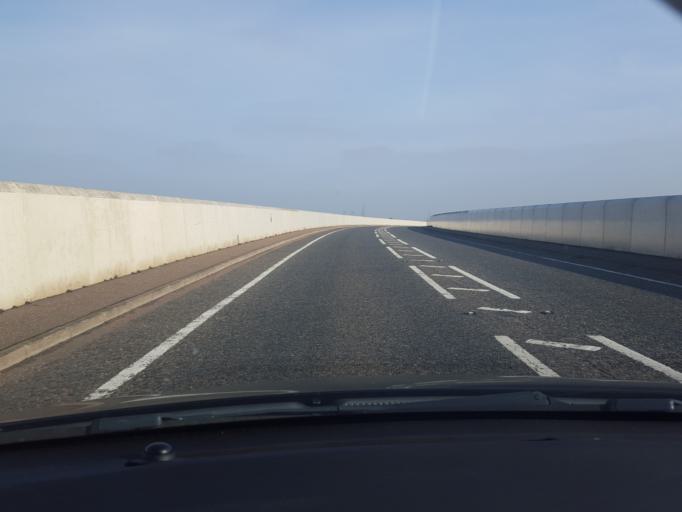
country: GB
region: England
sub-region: Essex
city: Dovercourt
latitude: 51.9400
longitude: 1.2638
